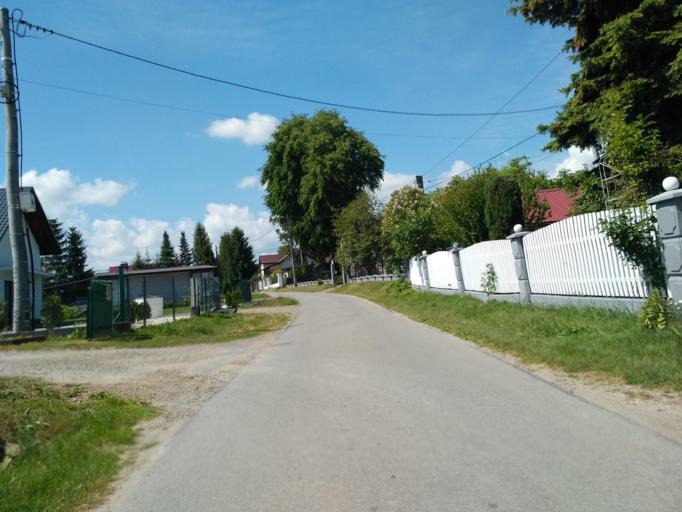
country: PL
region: Subcarpathian Voivodeship
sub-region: Powiat krosnienski
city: Miejsce Piastowe
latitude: 49.6485
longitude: 21.7596
